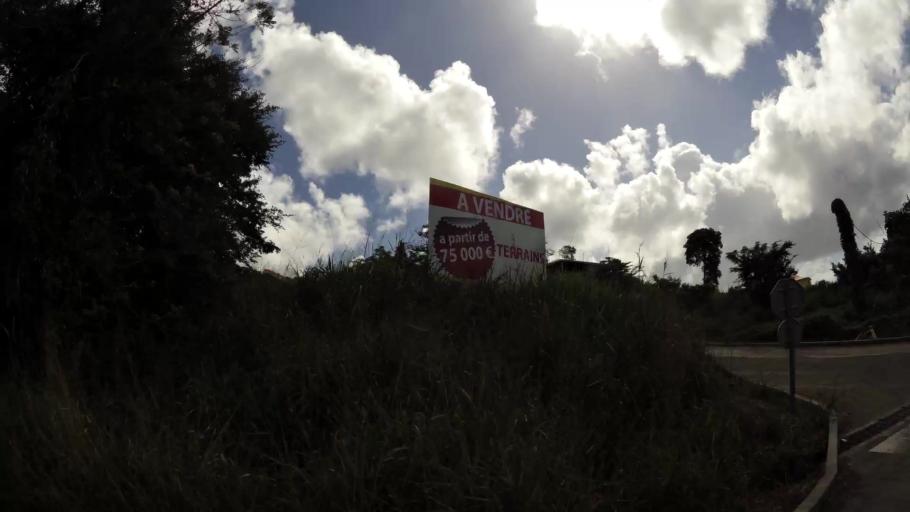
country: MQ
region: Martinique
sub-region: Martinique
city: Sainte-Luce
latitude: 14.4870
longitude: -60.9912
